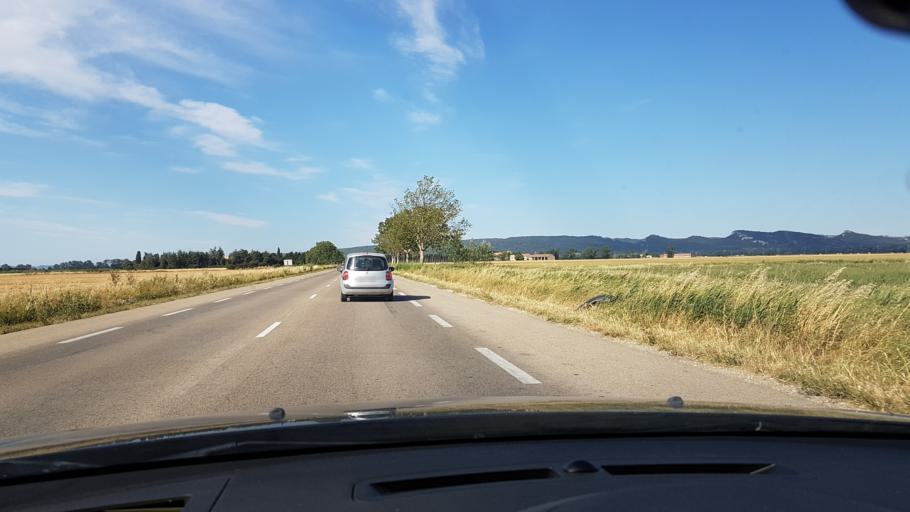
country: FR
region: Provence-Alpes-Cote d'Azur
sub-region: Departement des Bouches-du-Rhone
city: Fontvieille
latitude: 43.7300
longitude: 4.6622
